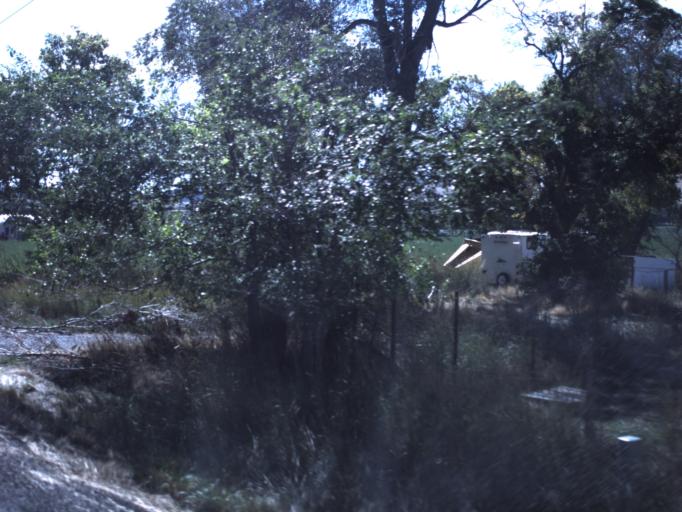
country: US
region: Utah
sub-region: Utah County
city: West Mountain
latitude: 40.0676
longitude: -111.7877
